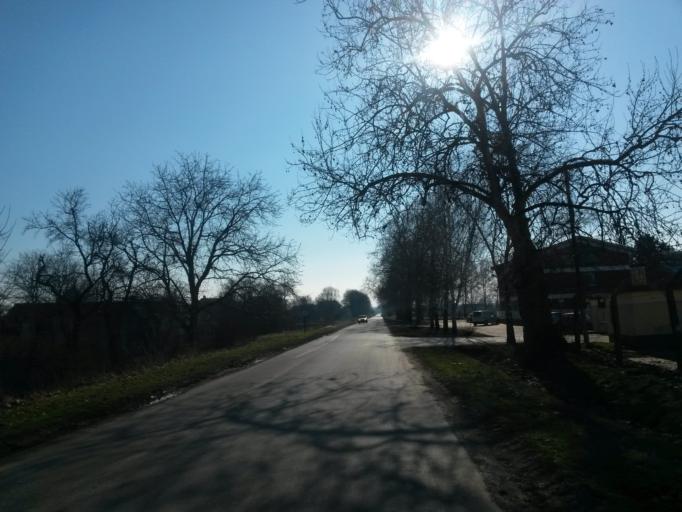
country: HR
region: Osjecko-Baranjska
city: Dalj
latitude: 45.4992
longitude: 18.9656
